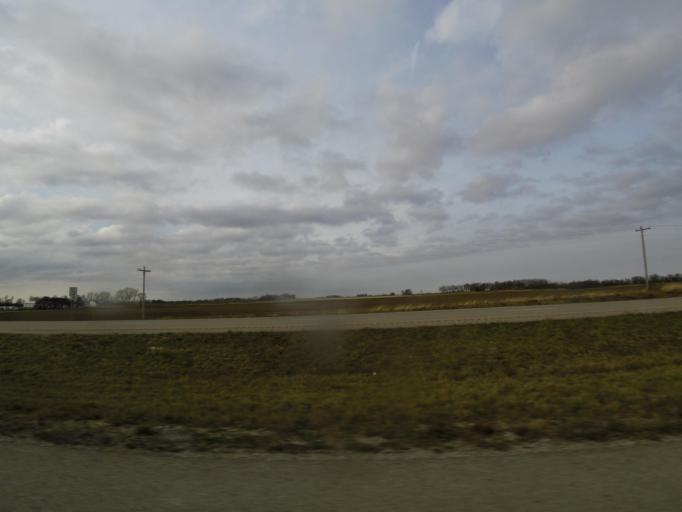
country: US
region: Illinois
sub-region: Christian County
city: Assumption
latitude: 39.4522
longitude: -89.0446
